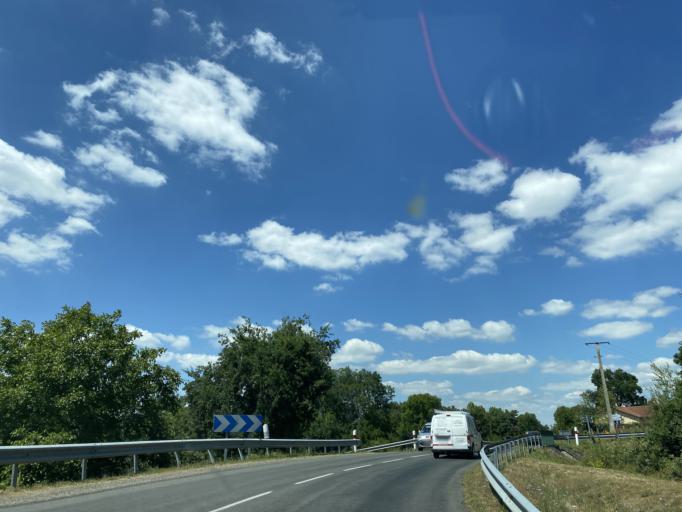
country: FR
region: Auvergne
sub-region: Departement du Puy-de-Dome
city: Peschadoires
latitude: 45.8655
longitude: 3.4960
